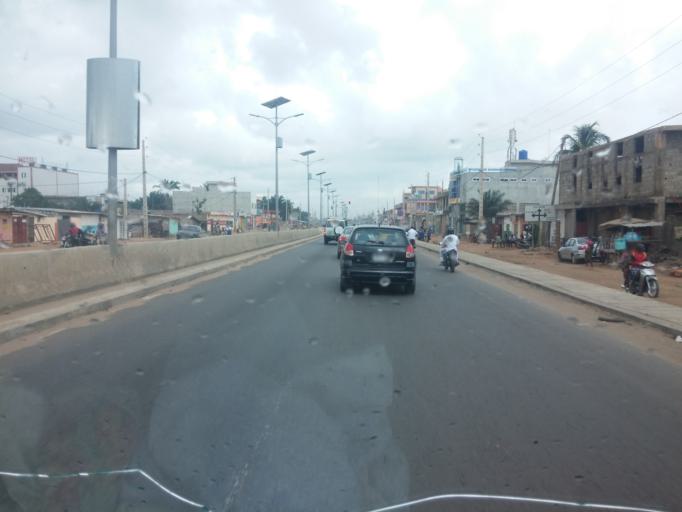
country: BJ
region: Atlantique
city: Hevie
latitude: 6.3889
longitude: 2.3145
